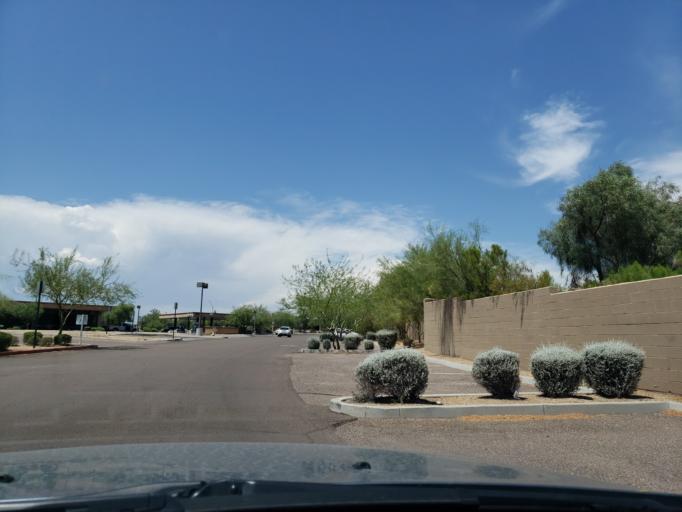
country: US
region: Arizona
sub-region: Maricopa County
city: Cave Creek
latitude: 33.7536
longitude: -111.9891
